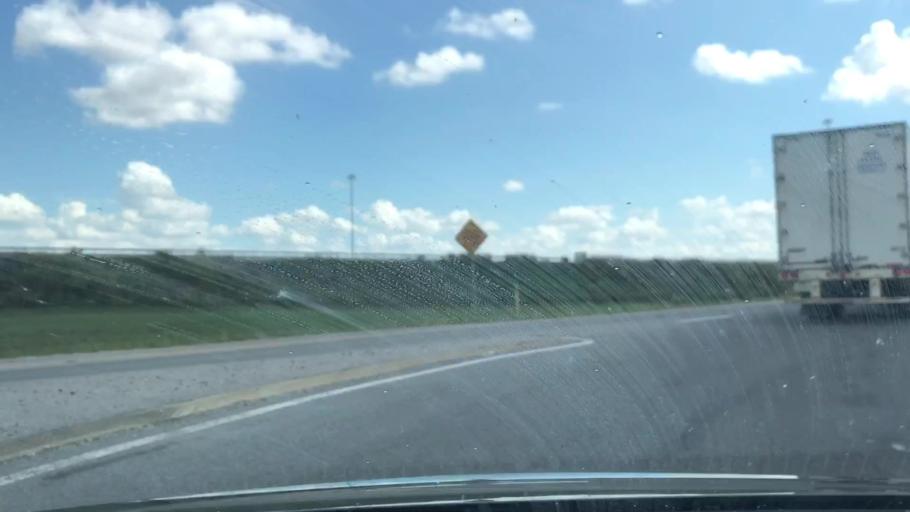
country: US
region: Kentucky
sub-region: Christian County
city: Hopkinsville
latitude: 36.8181
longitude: -87.4847
